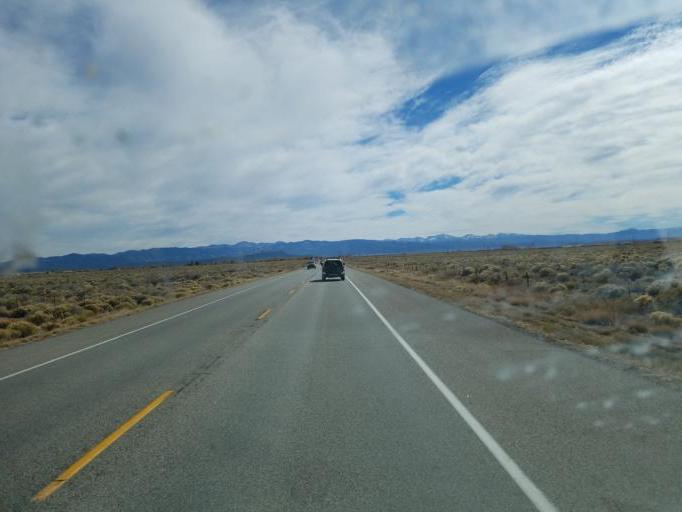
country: US
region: Colorado
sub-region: Costilla County
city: San Luis
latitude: 37.4436
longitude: -105.5319
